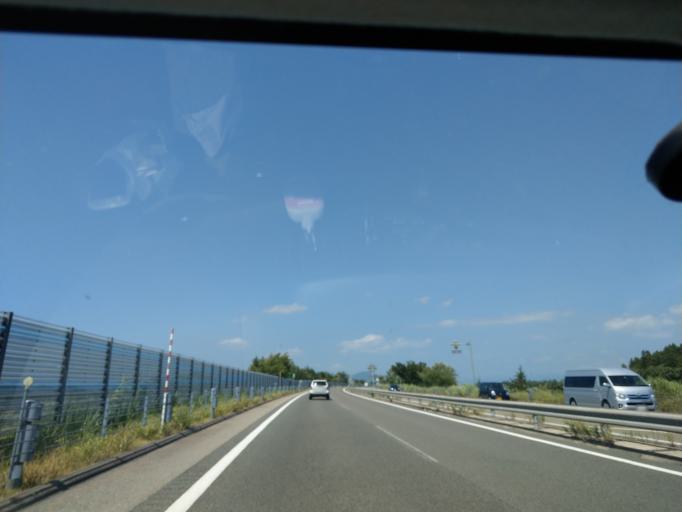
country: JP
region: Akita
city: Yokotemachi
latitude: 39.3595
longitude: 140.4901
